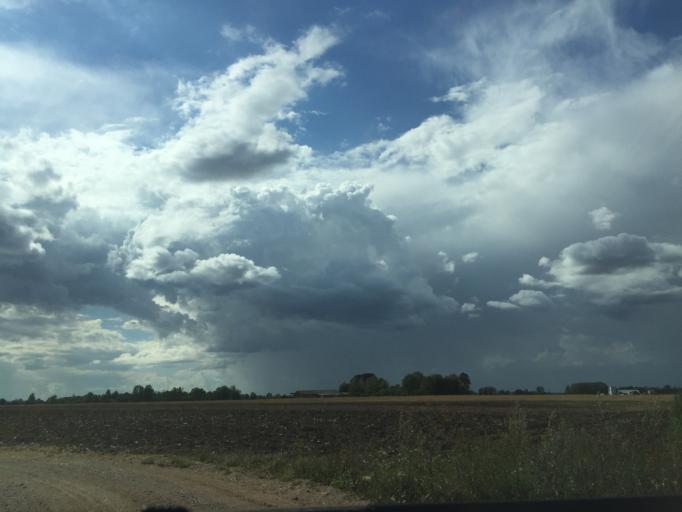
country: LT
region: Siauliu apskritis
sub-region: Joniskis
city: Joniskis
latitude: 56.3589
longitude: 23.5825
